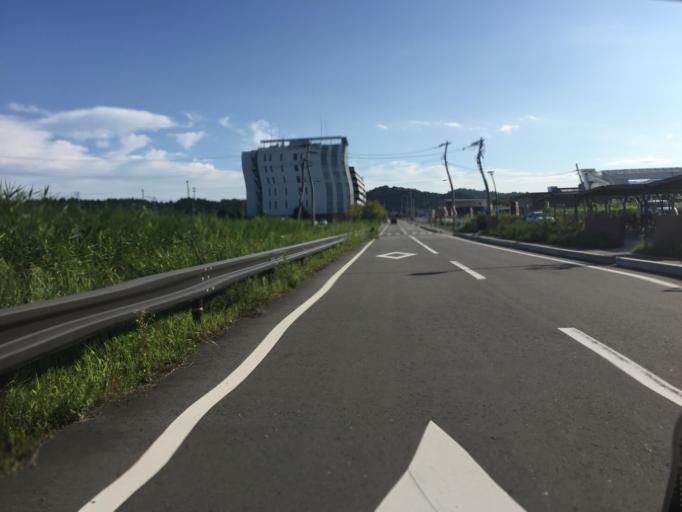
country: JP
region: Fukushima
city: Iwaki
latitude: 37.2134
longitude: 141.0012
